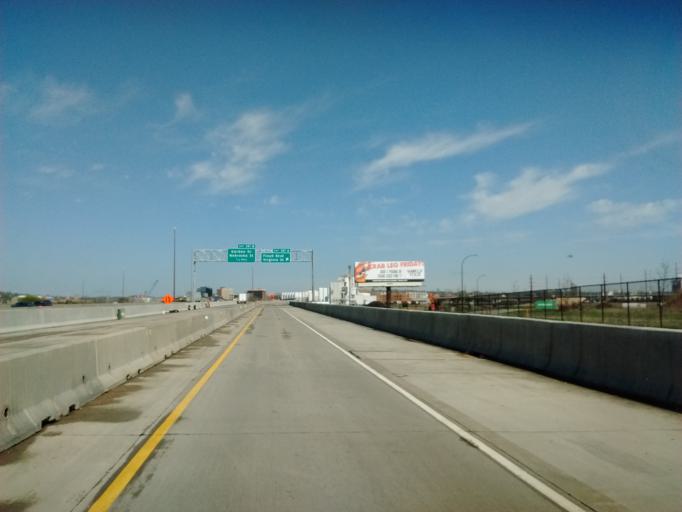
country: US
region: Iowa
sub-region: Woodbury County
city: Sioux City
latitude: 42.4821
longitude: -96.3895
